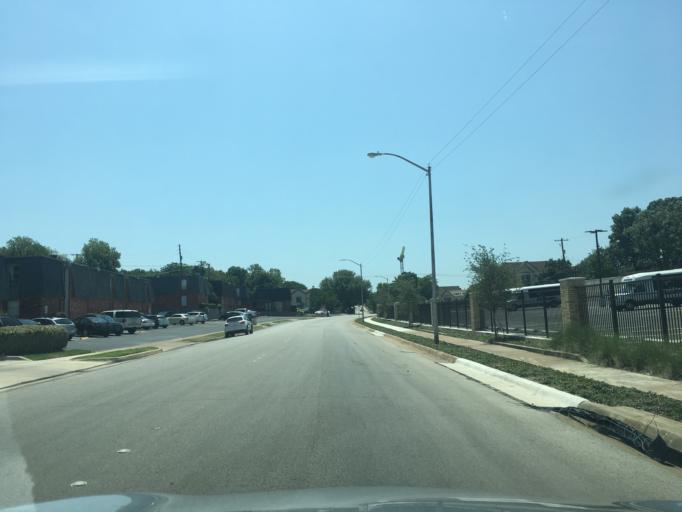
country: US
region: Texas
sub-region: Tarrant County
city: Fort Worth
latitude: 32.7112
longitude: -97.3532
